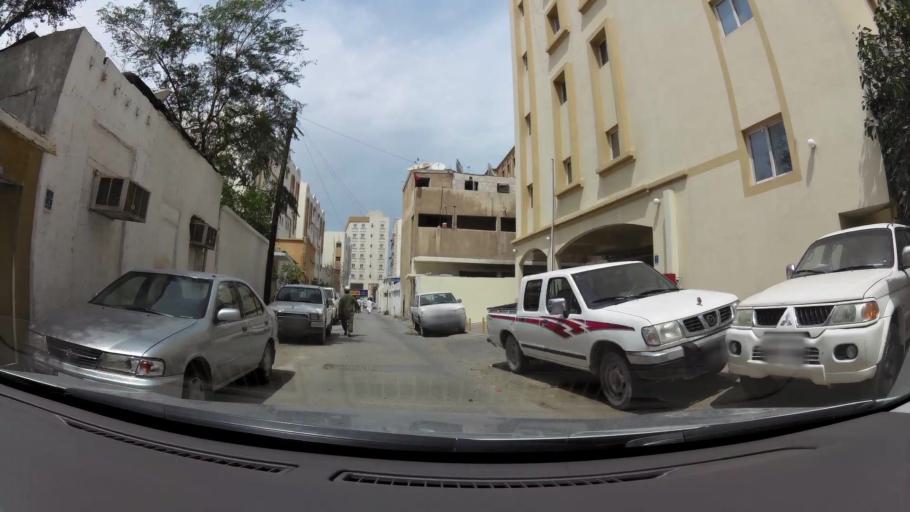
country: QA
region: Baladiyat ad Dawhah
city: Doha
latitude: 25.2754
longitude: 51.5228
